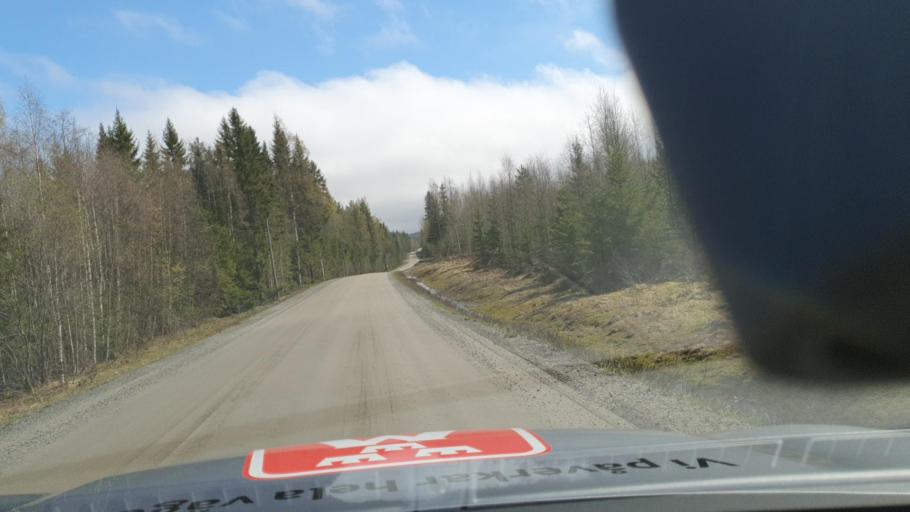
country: SE
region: Vaesterbotten
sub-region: Bjurholms Kommun
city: Bjurholm
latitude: 63.6825
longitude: 18.9819
